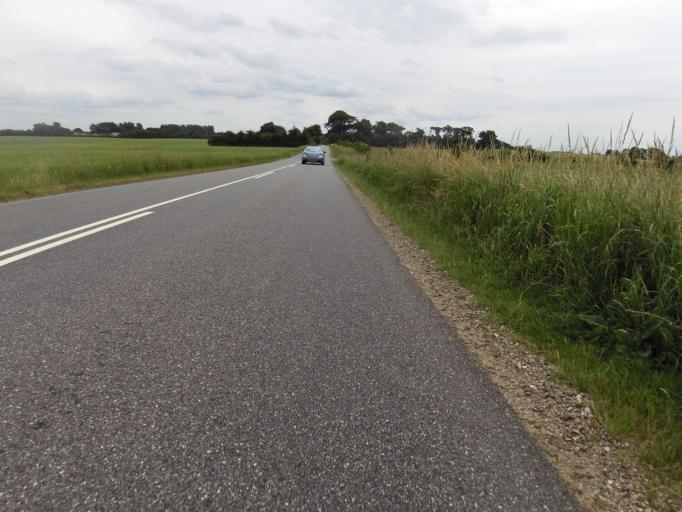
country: DK
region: Central Jutland
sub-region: Holstebro Kommune
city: Vinderup
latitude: 56.4122
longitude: 8.7072
